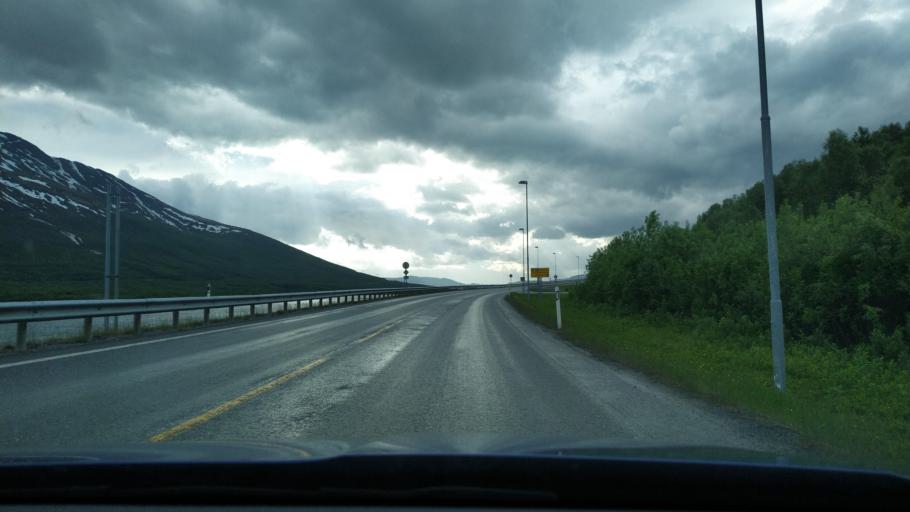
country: NO
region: Troms
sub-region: Balsfjord
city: Storsteinnes
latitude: 69.2223
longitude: 19.5162
